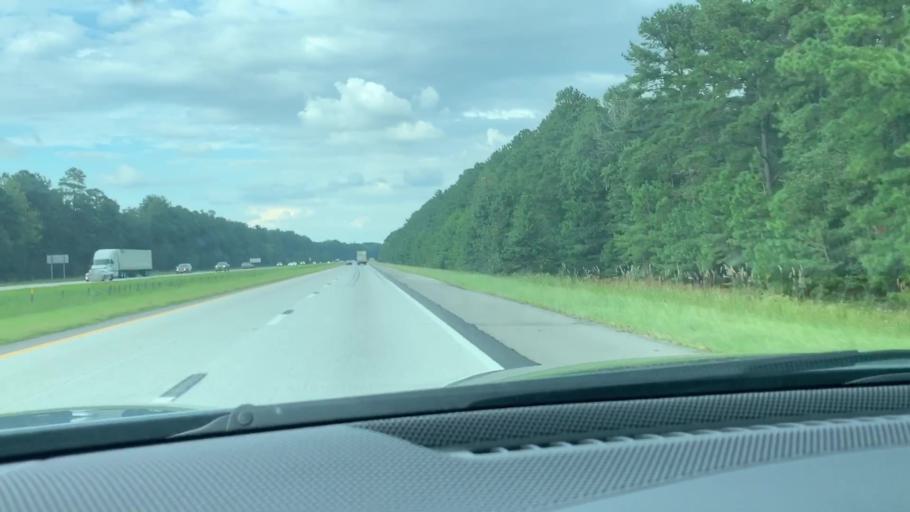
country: US
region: South Carolina
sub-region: Dorchester County
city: Saint George
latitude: 33.3014
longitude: -80.5557
